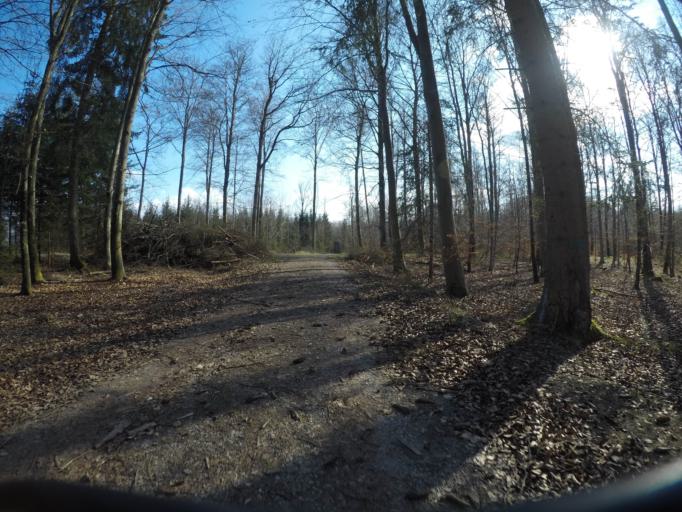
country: DE
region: Baden-Wuerttemberg
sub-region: Tuebingen Region
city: Dusslingen
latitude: 48.4634
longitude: 9.0270
